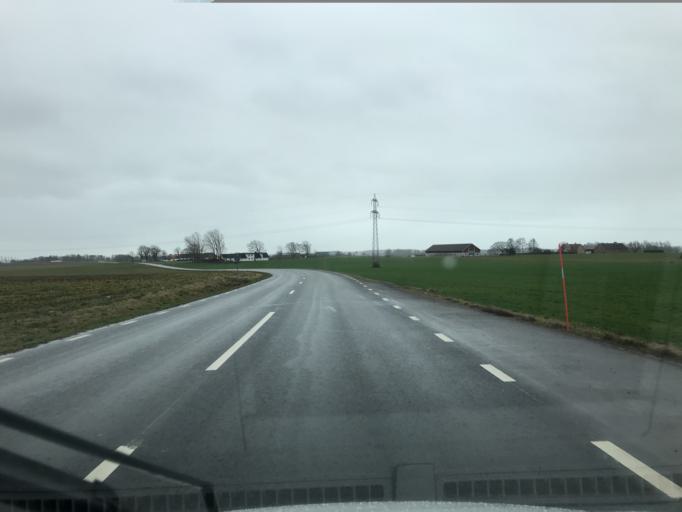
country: SE
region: Skane
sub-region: Bastads Kommun
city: Forslov
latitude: 56.3321
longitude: 12.8884
